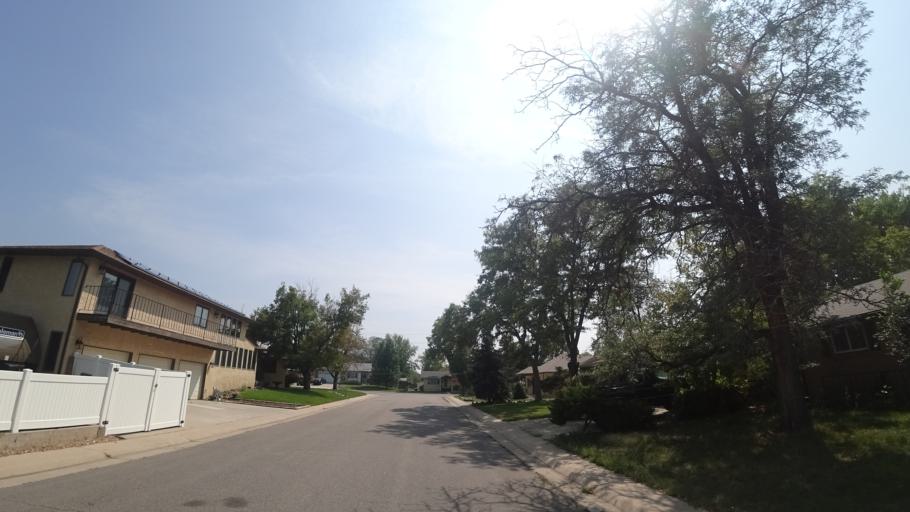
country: US
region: Colorado
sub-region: Arapahoe County
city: Englewood
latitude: 39.6338
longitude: -105.0025
